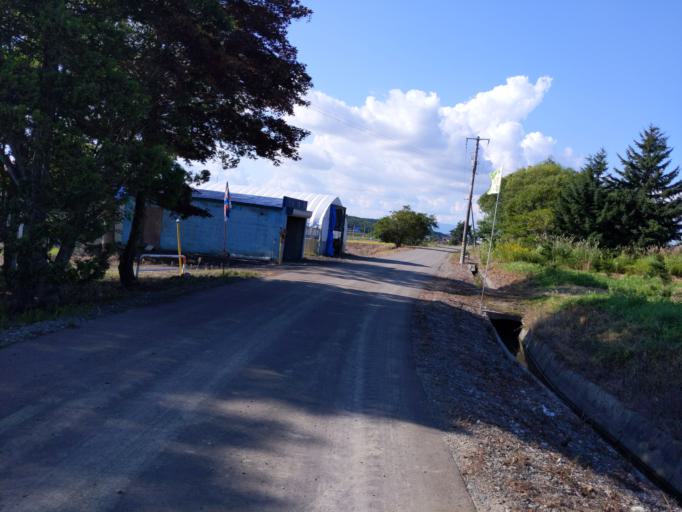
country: JP
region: Hokkaido
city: Iwamizawa
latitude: 43.1953
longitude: 141.8293
